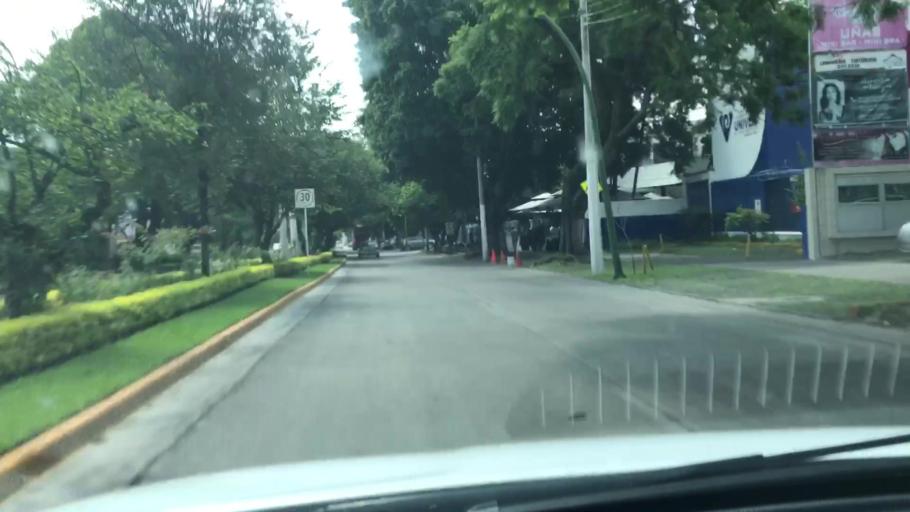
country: MX
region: Jalisco
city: Guadalajara
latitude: 20.6607
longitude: -103.3992
